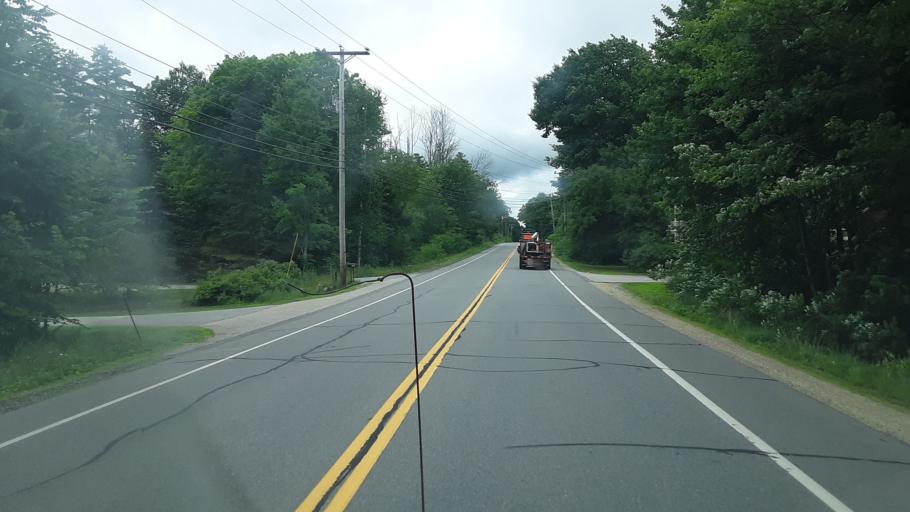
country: US
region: New Hampshire
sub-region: Rockingham County
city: Northwood
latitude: 43.1834
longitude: -71.1289
